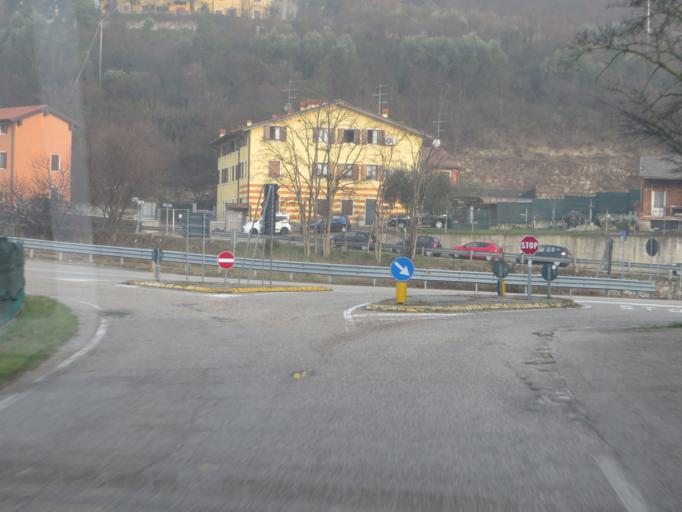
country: IT
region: Veneto
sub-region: Provincia di Verona
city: Pastrengo
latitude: 45.4827
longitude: 10.8063
